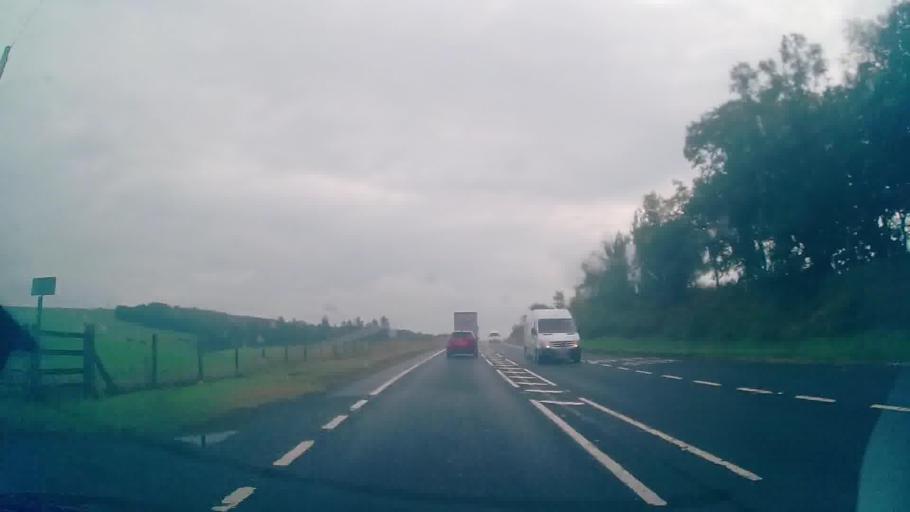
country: GB
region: Scotland
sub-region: Dumfries and Galloway
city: Lochmaben
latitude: 55.0407
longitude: -3.4399
